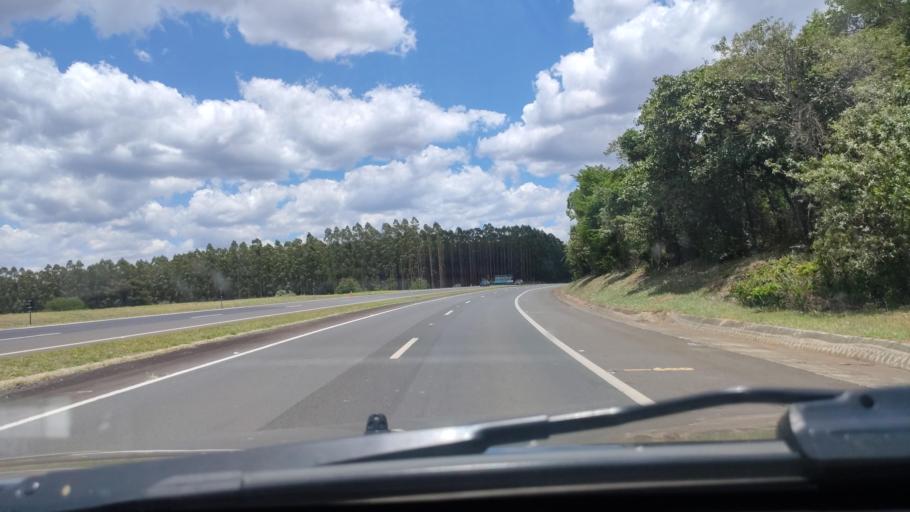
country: BR
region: Sao Paulo
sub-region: Duartina
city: Duartina
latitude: -22.4870
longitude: -49.2422
